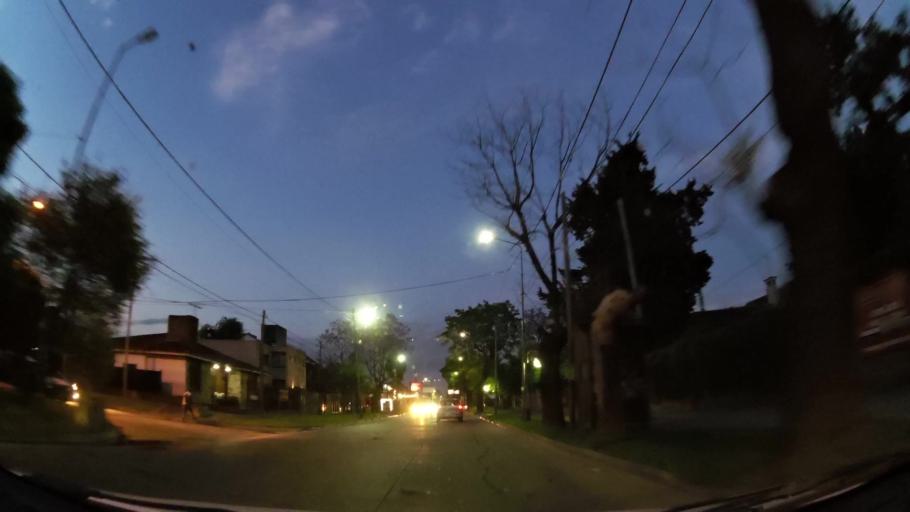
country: AR
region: Buenos Aires
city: Ituzaingo
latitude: -34.6505
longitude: -58.6584
